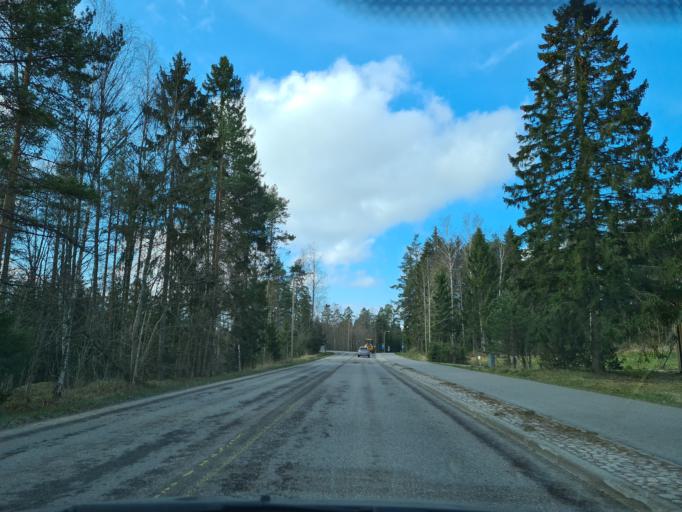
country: FI
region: Uusimaa
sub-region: Helsinki
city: Kirkkonummi
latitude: 60.0852
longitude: 24.4068
